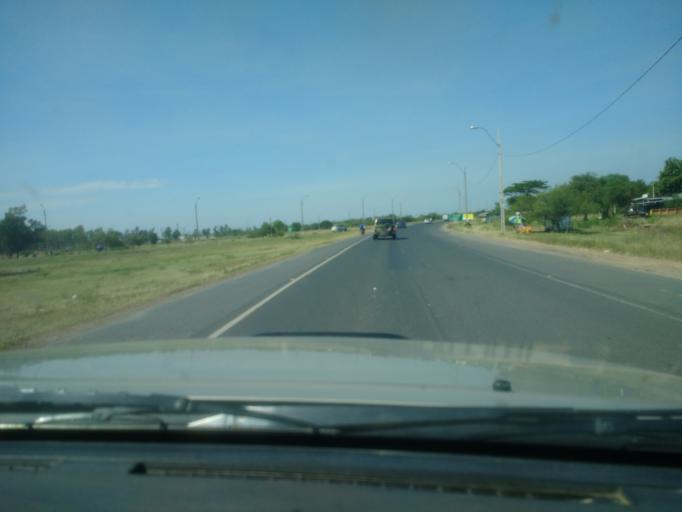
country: PY
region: Central
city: Colonia Mariano Roque Alonso
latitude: -25.1682
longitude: -57.5631
